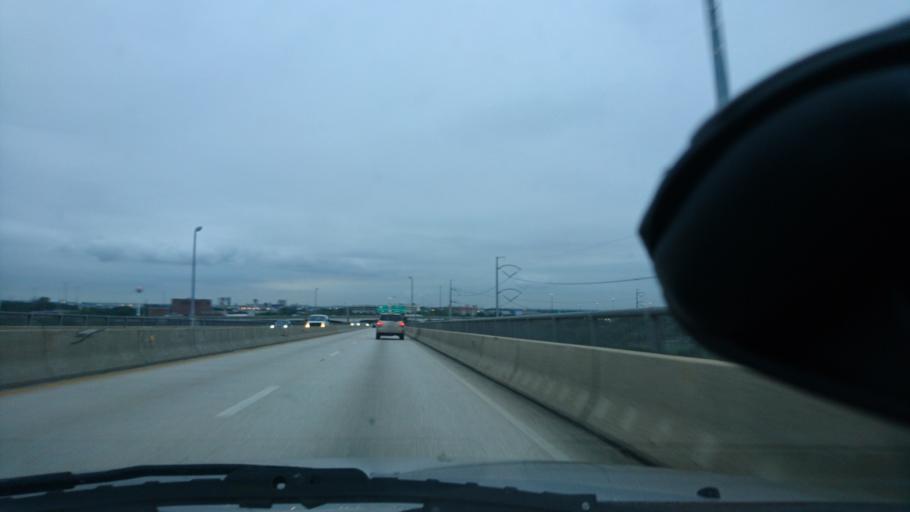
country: US
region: Pennsylvania
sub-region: Delaware County
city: Colwyn
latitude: 39.8945
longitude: -75.2192
